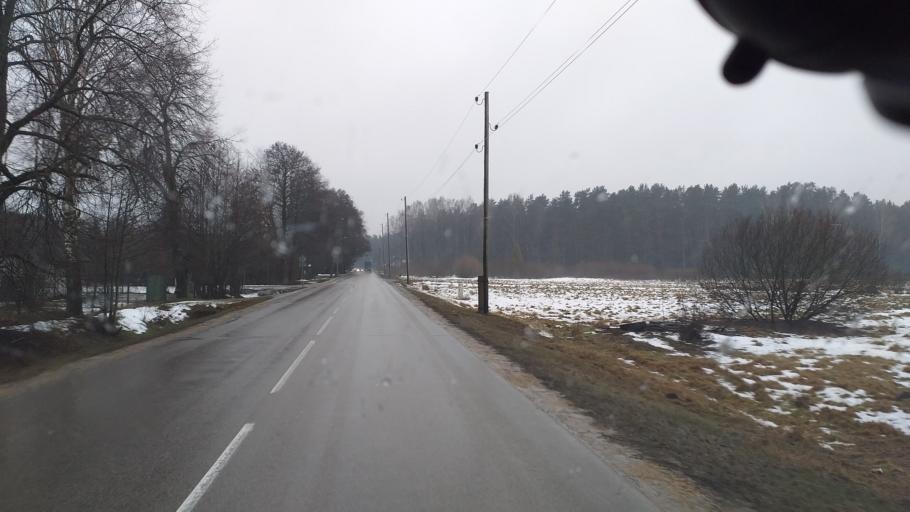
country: LV
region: Babite
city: Pinki
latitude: 56.9667
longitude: 23.9657
